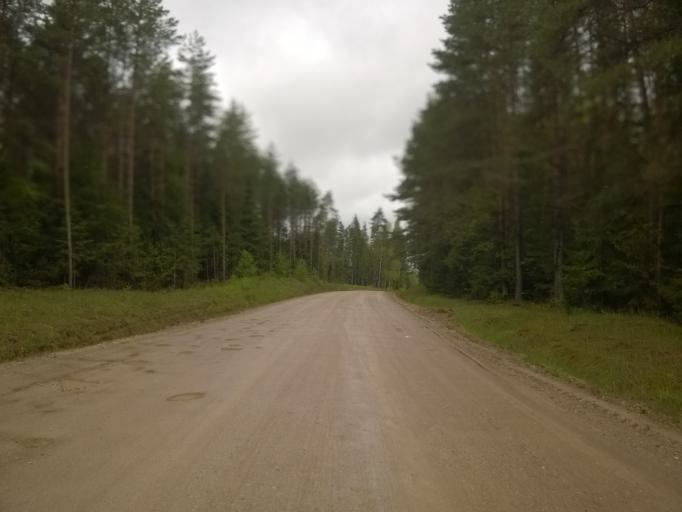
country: LV
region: Amatas Novads
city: Drabesi
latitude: 57.2151
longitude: 25.2321
